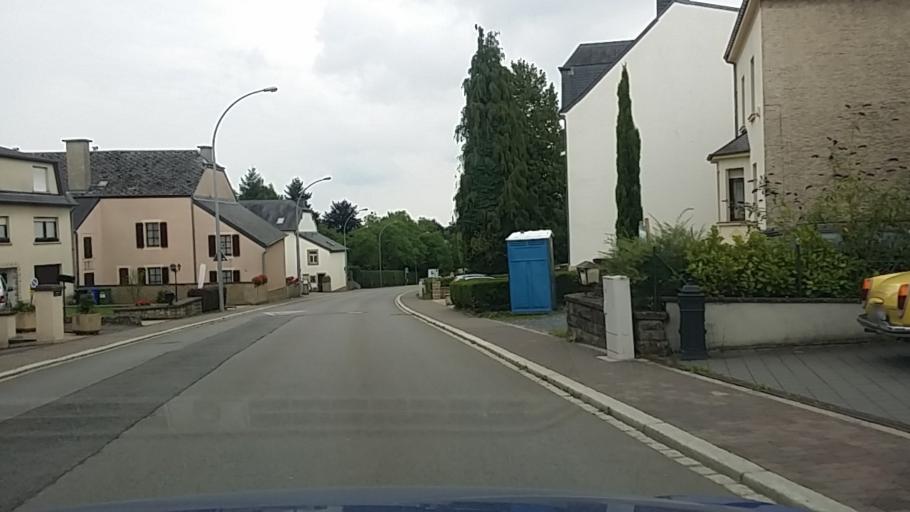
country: LU
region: Luxembourg
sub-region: Canton de Luxembourg
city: Bertrange
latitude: 49.6172
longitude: 6.0483
